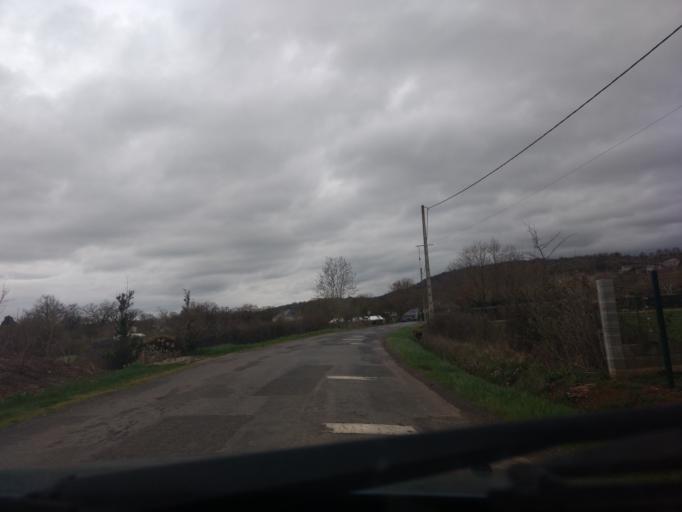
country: FR
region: Midi-Pyrenees
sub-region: Departement de l'Aveyron
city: La Loubiere
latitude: 44.3927
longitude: 2.6927
